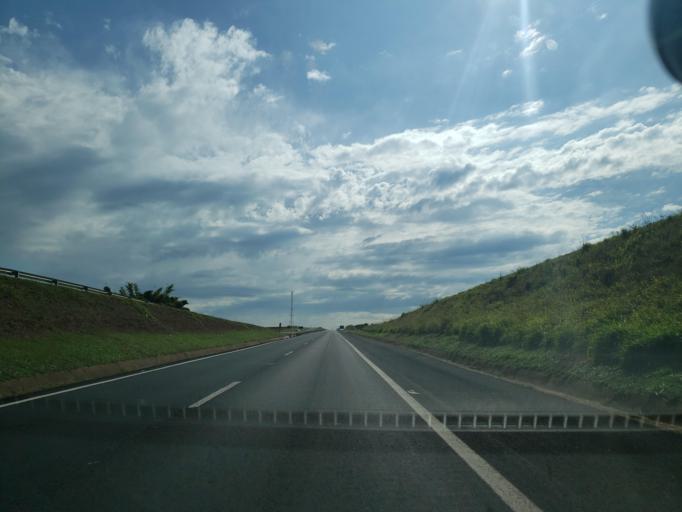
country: BR
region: Sao Paulo
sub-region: Cafelandia
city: Cafelandia
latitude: -21.8878
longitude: -49.5452
